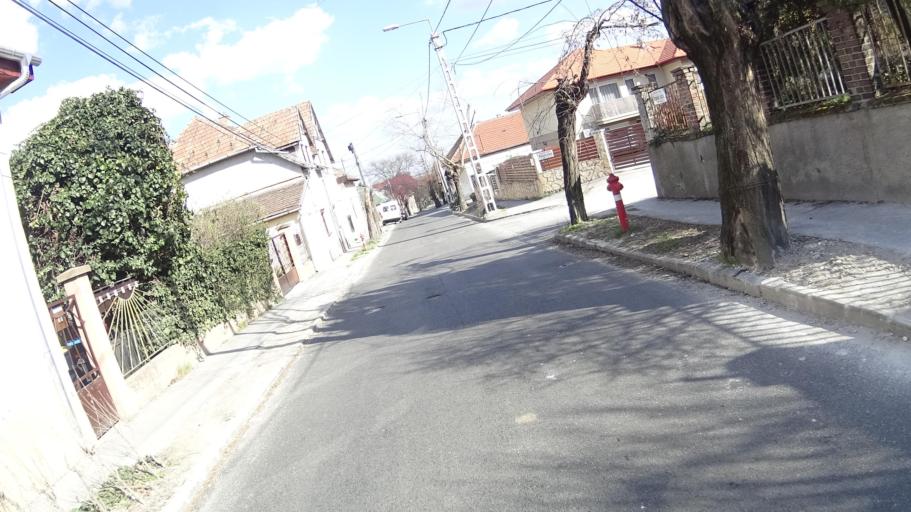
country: HU
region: Budapest
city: Budapest XXII. keruelet
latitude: 47.4257
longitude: 19.0313
